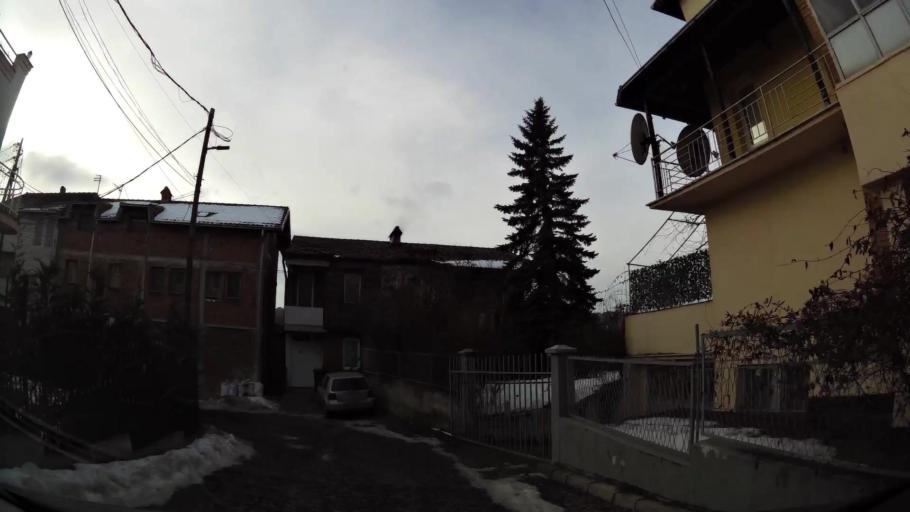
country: XK
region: Pristina
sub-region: Komuna e Prishtines
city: Pristina
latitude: 42.6670
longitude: 21.1785
